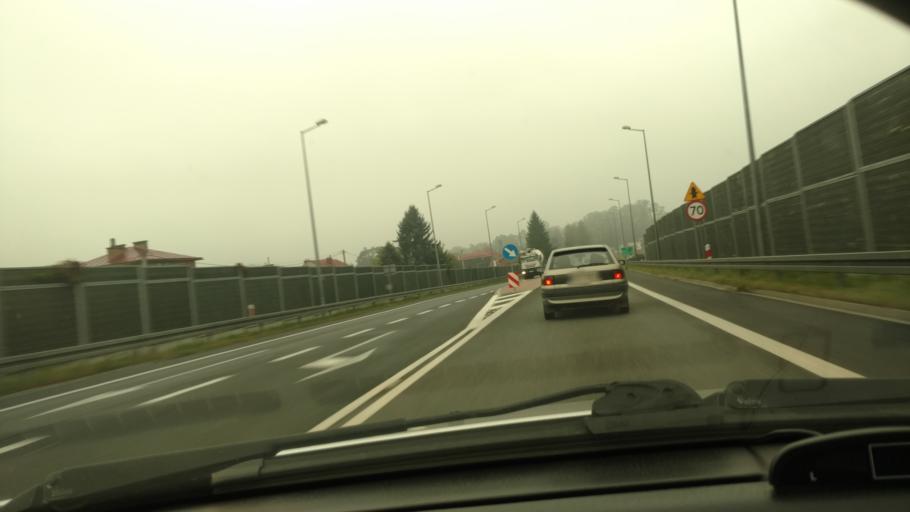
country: PL
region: Lesser Poland Voivodeship
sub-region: Powiat gorlicki
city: Biecz
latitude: 49.7072
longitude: 21.2392
